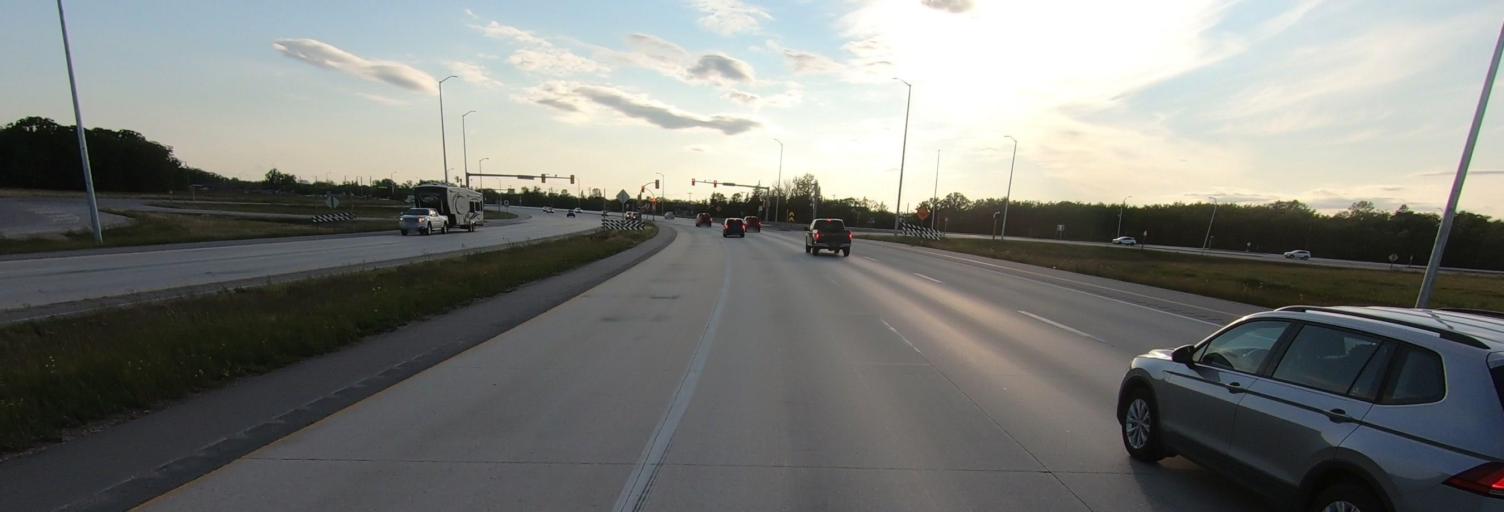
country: CA
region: Manitoba
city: Winnipeg
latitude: 49.9669
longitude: -97.0112
